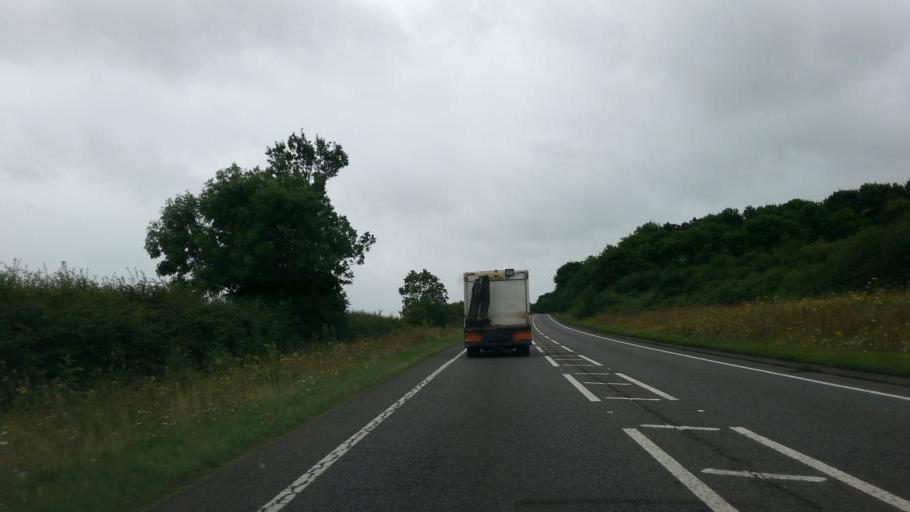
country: GB
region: England
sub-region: Northamptonshire
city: Oundle
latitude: 52.4483
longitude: -0.4648
